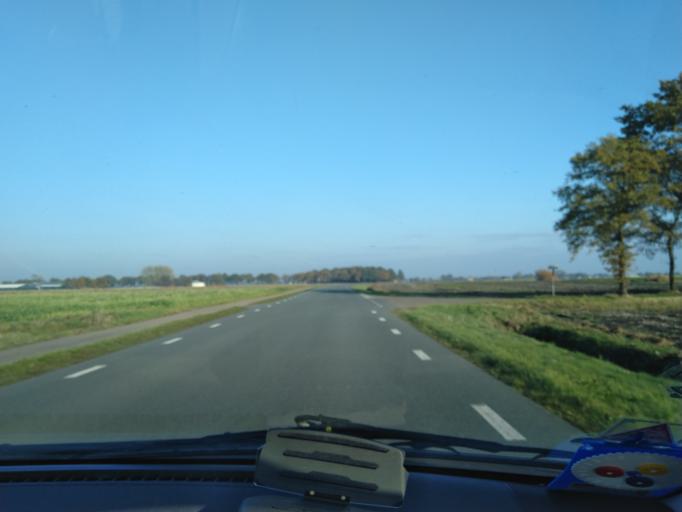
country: NL
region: Groningen
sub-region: Gemeente Hoogezand-Sappemeer
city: Hoogezand
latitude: 53.1185
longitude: 6.7509
